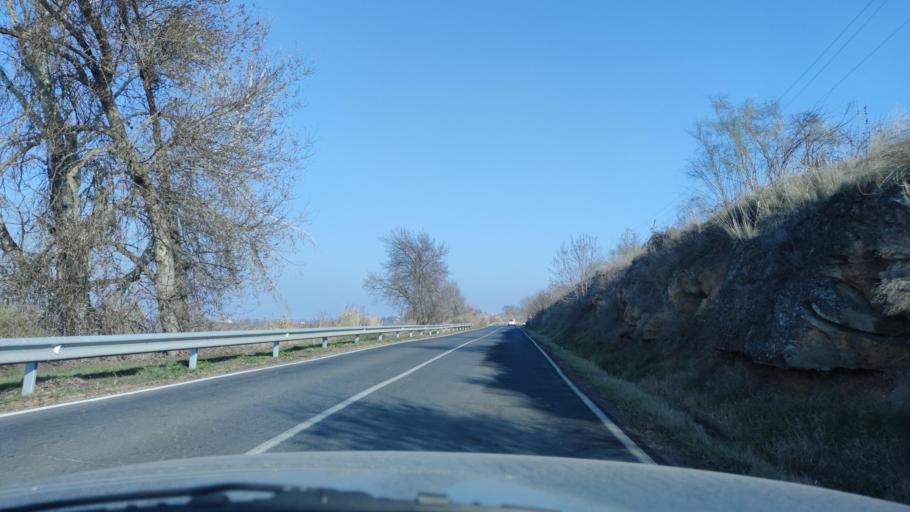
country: ES
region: Catalonia
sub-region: Provincia de Lleida
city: Sunyer
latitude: 41.5611
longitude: 0.5760
